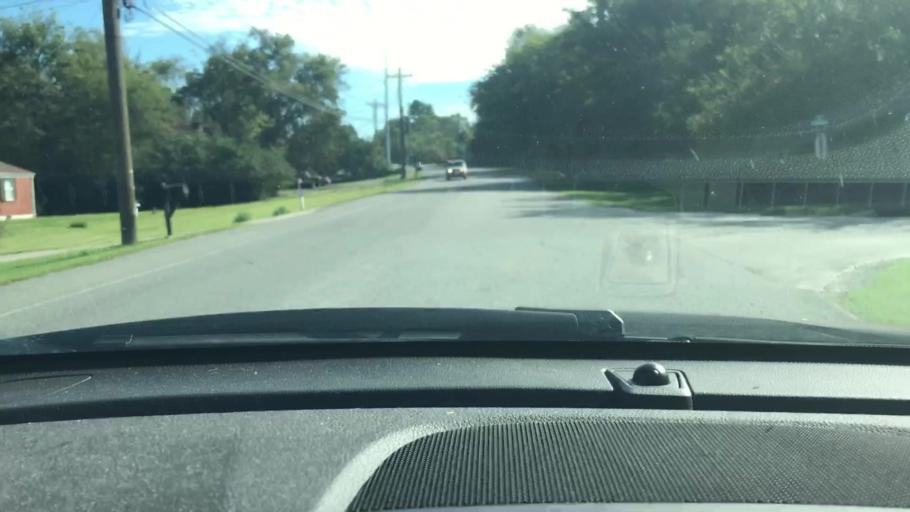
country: US
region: Tennessee
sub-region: Sumner County
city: Hendersonville
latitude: 36.3009
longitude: -86.6395
